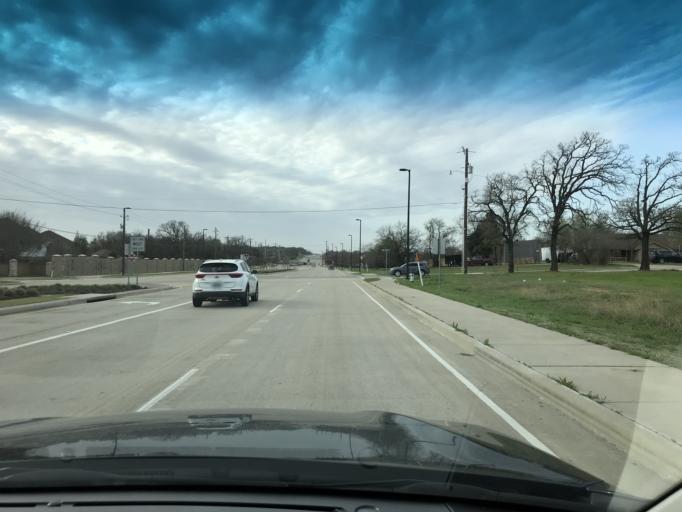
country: US
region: Texas
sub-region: Tarrant County
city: Southlake
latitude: 32.9421
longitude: -97.1860
